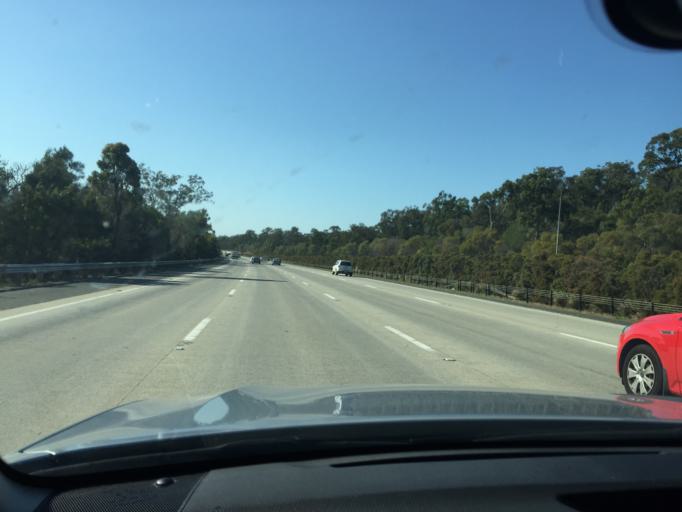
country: AU
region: Queensland
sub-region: Gold Coast
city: Ormeau Hills
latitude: -27.8108
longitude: 153.2707
